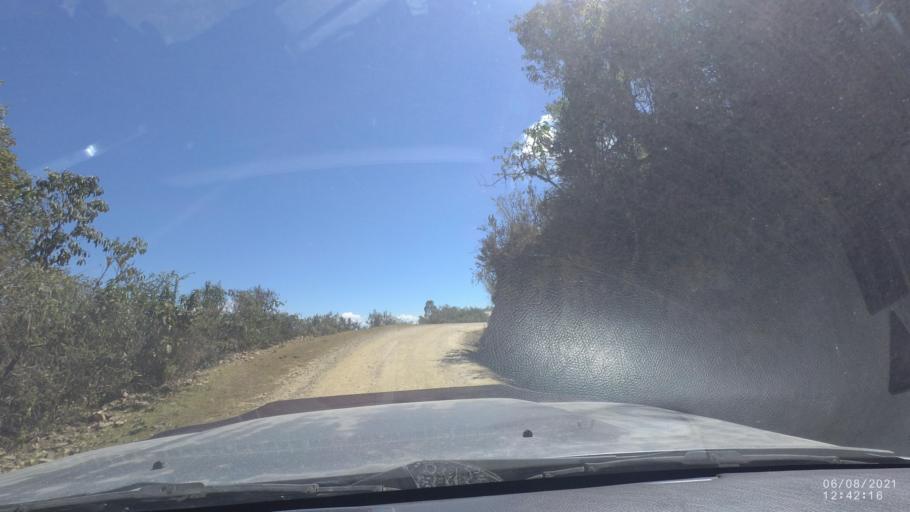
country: BO
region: Cochabamba
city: Colchani
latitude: -16.7786
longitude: -66.6657
